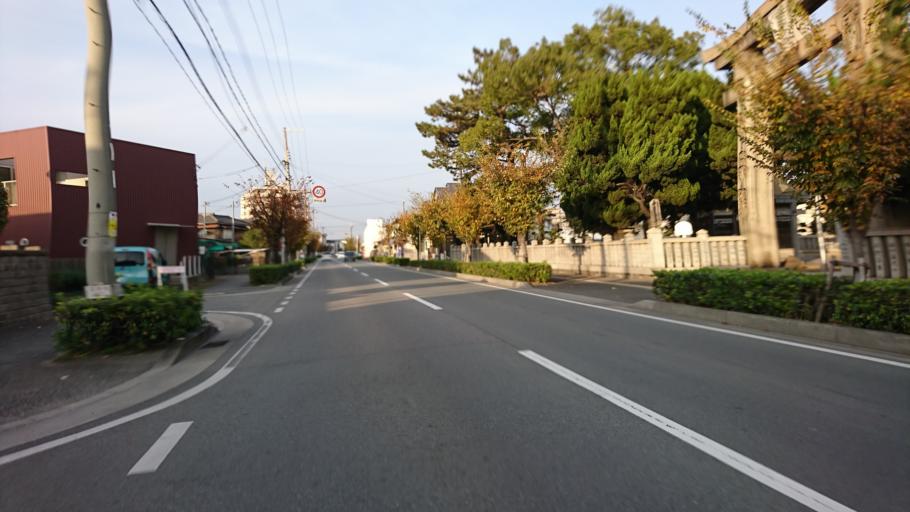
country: JP
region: Hyogo
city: Kakogawacho-honmachi
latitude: 34.7231
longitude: 134.8455
